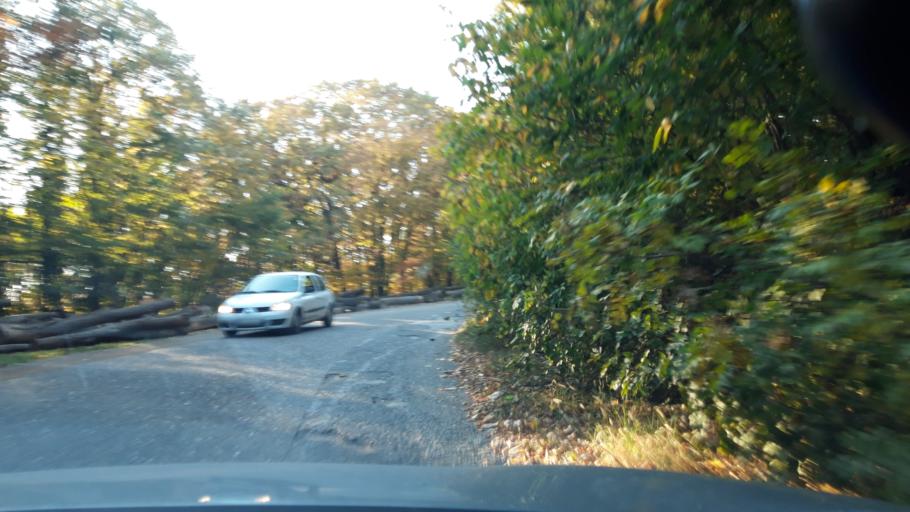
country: RS
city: Vrdnik
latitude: 45.1547
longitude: 19.8112
